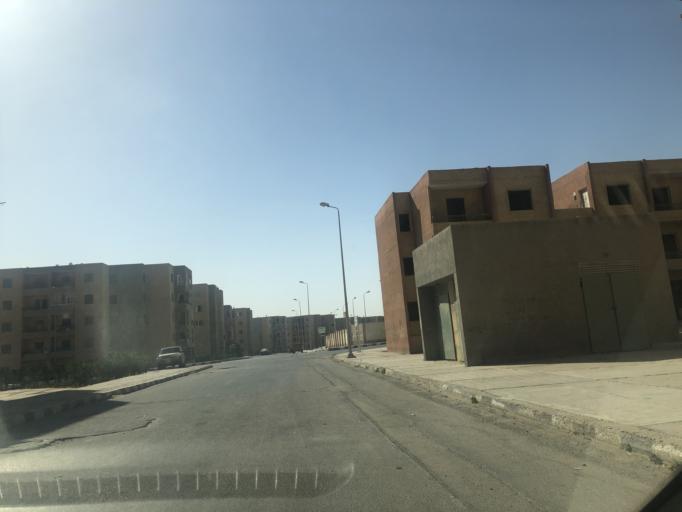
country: EG
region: Al Jizah
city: Madinat Sittah Uktubar
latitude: 29.9239
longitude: 30.9353
